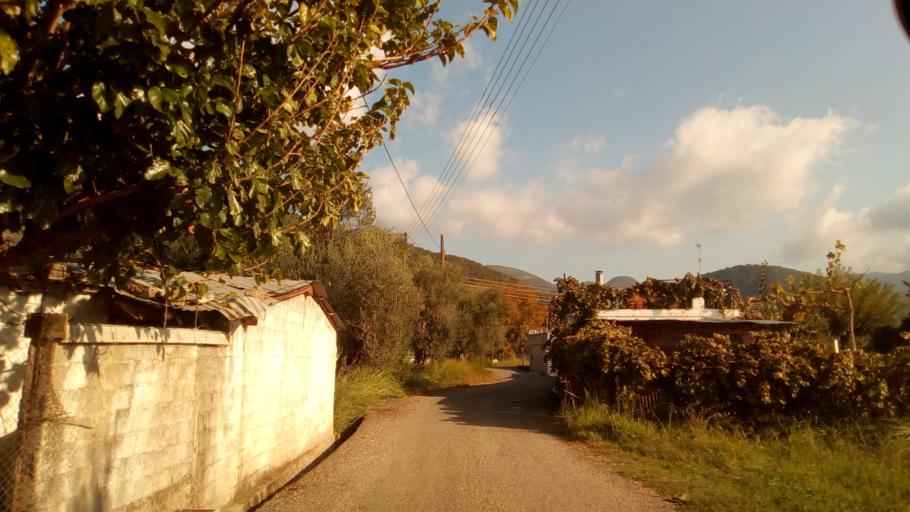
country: GR
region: West Greece
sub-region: Nomos Aitolias kai Akarnanias
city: Nafpaktos
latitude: 38.4166
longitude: 21.8893
